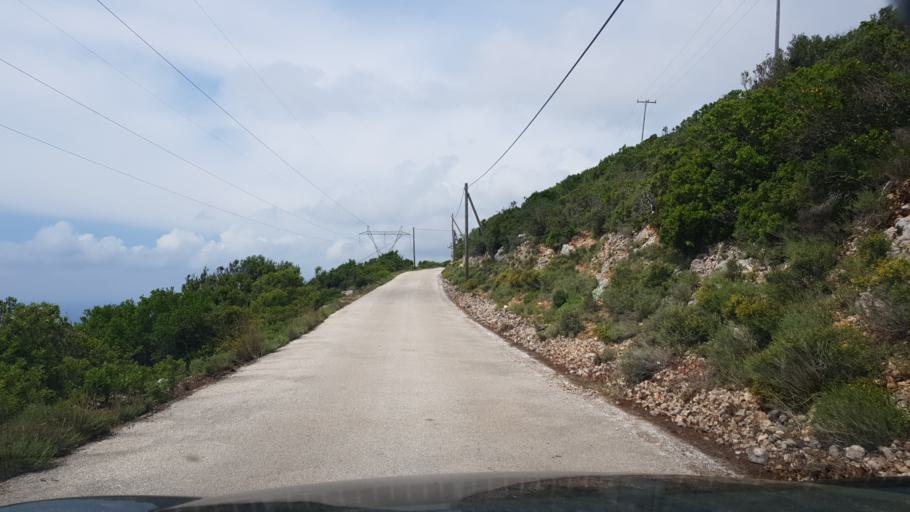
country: GR
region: Ionian Islands
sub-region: Lefkada
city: Nidri
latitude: 38.6045
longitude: 20.5605
